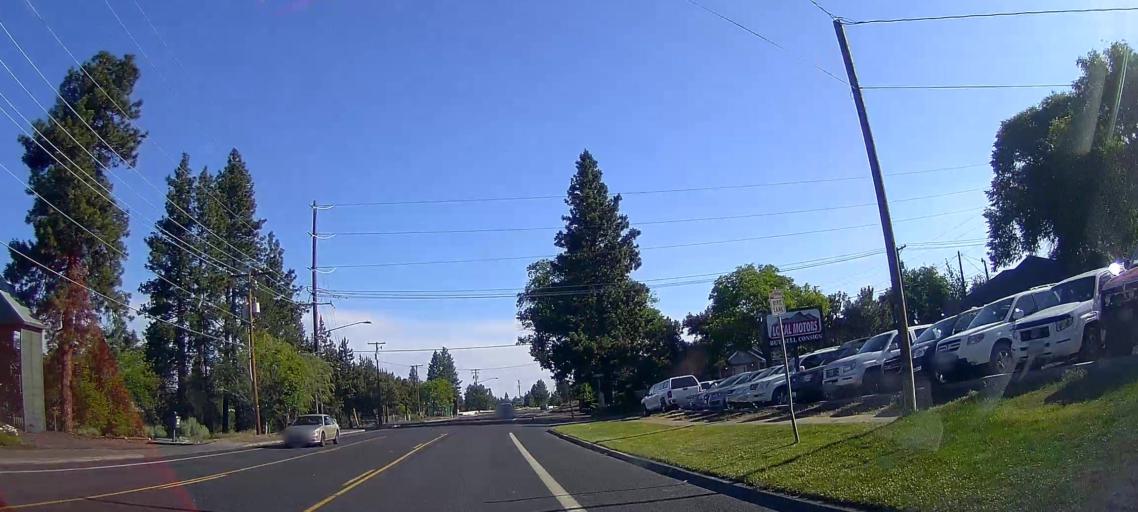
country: US
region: Oregon
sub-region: Deschutes County
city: Bend
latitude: 44.0742
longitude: -121.3058
